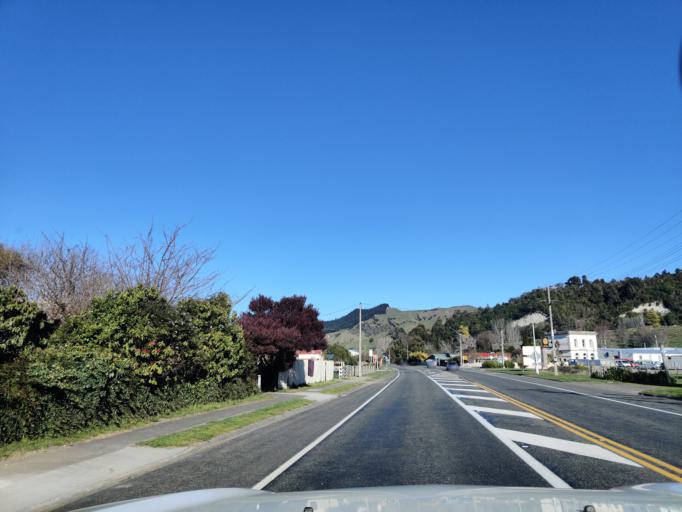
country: NZ
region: Manawatu-Wanganui
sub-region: Ruapehu District
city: Waiouru
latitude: -39.8089
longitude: 175.7900
